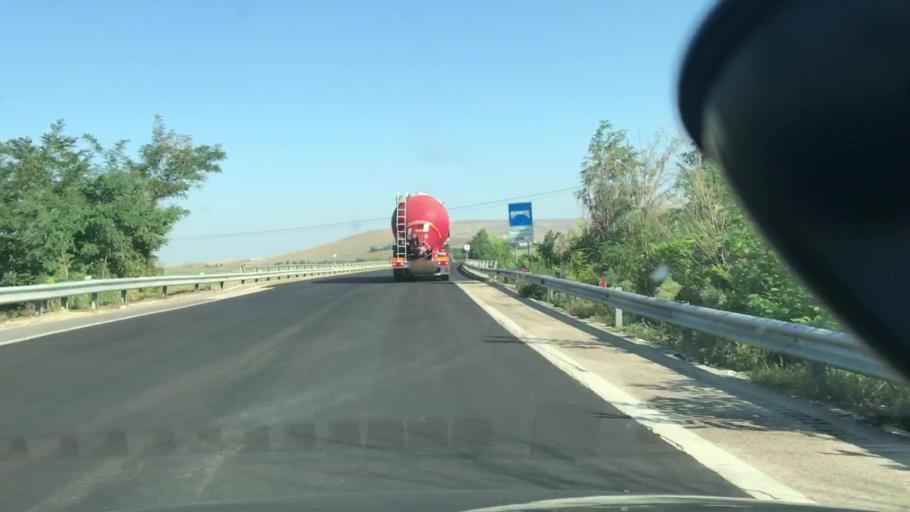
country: IT
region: Basilicate
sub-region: Provincia di Matera
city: Irsina
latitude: 40.7974
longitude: 16.2752
